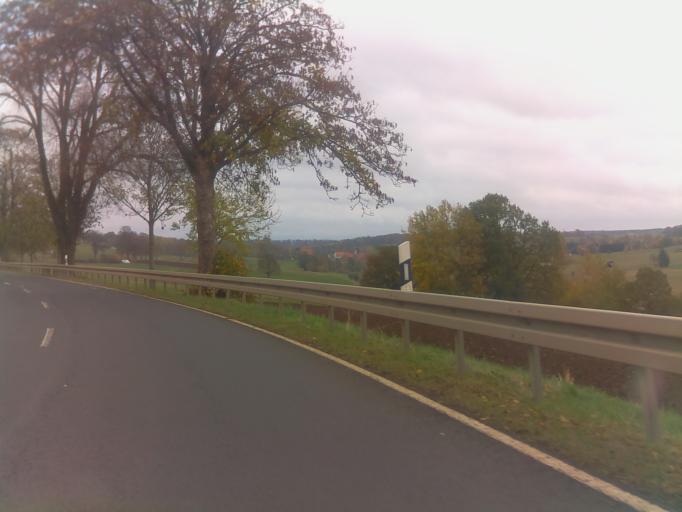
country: DE
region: Hesse
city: Herbstein
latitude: 50.5375
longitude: 9.3607
